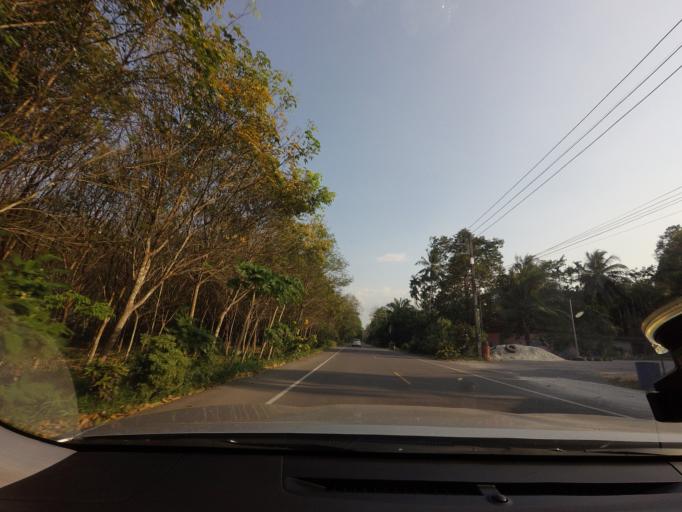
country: TH
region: Surat Thani
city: Phrasaeng
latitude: 8.5770
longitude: 99.2811
